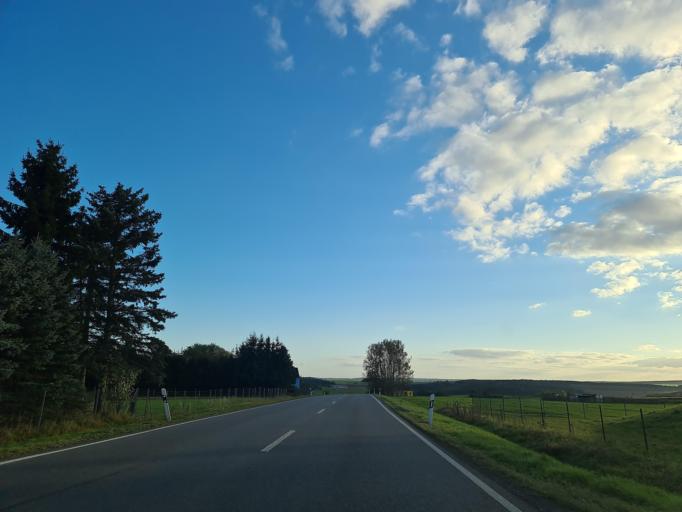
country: DE
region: Thuringia
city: Wildetaube
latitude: 50.7222
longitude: 12.1096
